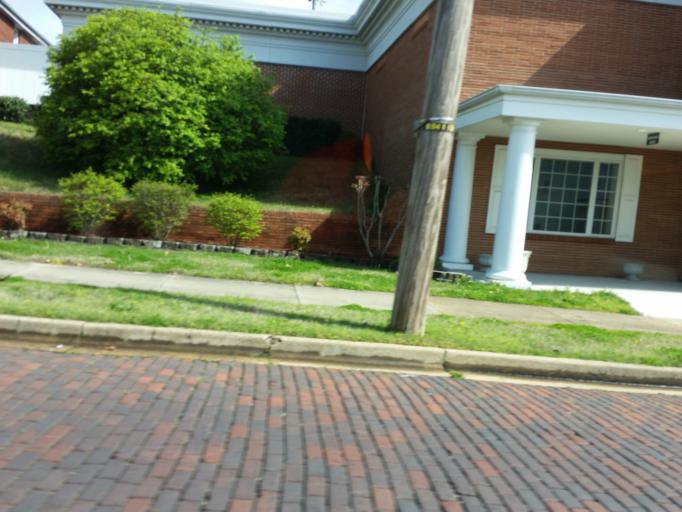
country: US
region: Missouri
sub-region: Butler County
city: Poplar Bluff
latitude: 36.7573
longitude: -90.3994
